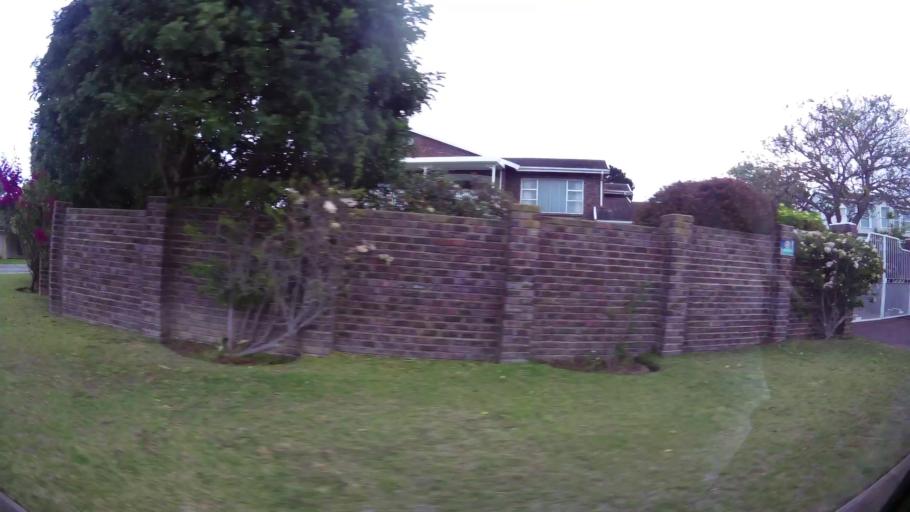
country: ZA
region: Western Cape
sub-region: Eden District Municipality
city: Plettenberg Bay
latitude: -34.0480
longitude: 23.3650
